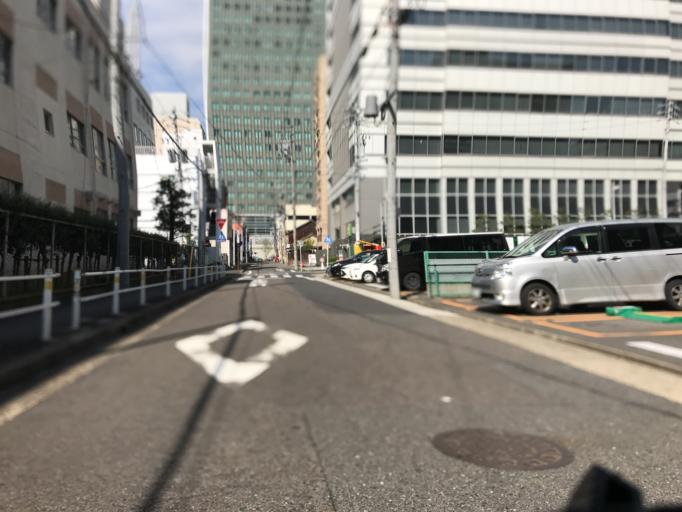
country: JP
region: Aichi
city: Nagoya-shi
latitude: 35.1733
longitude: 136.9124
